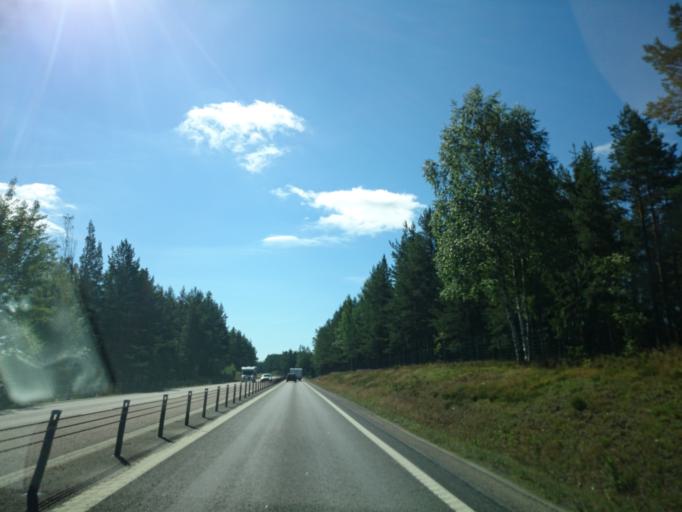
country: SE
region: Gaevleborg
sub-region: Gavle Kommun
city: Norrsundet
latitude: 60.9992
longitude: 16.9927
